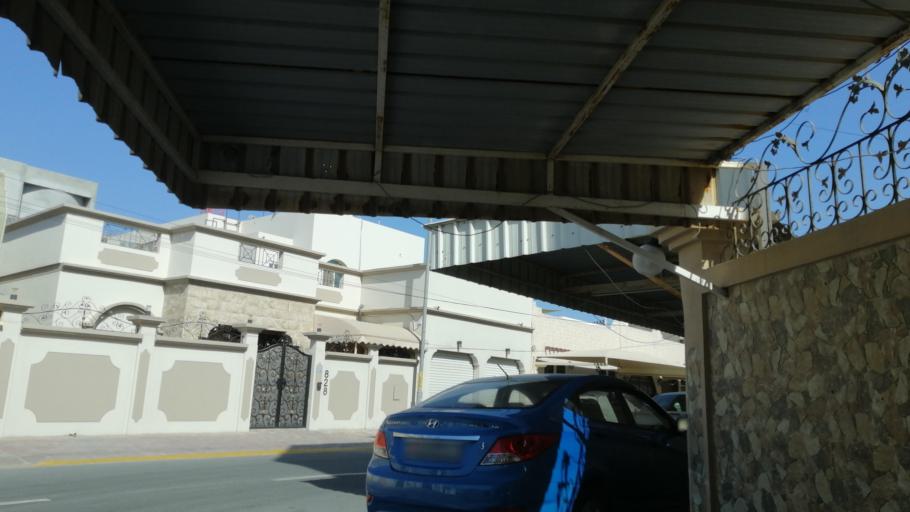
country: BH
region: Muharraq
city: Al Hadd
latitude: 26.2551
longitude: 50.6367
